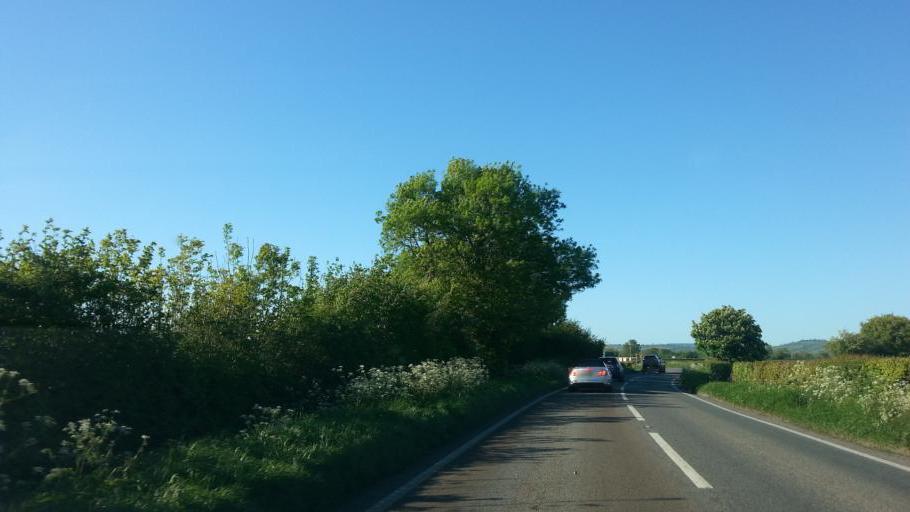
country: GB
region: England
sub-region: Somerset
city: Castle Cary
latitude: 51.1114
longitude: -2.5200
